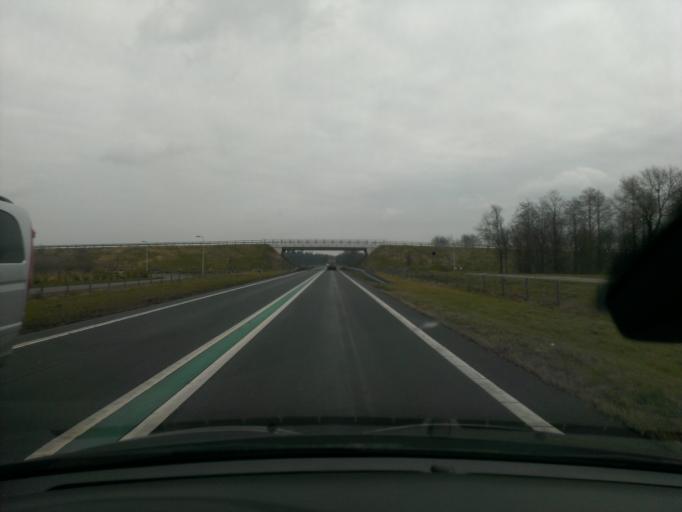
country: NL
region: Overijssel
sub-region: Gemeente Twenterand
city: Magele
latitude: 52.5598
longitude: 6.5064
